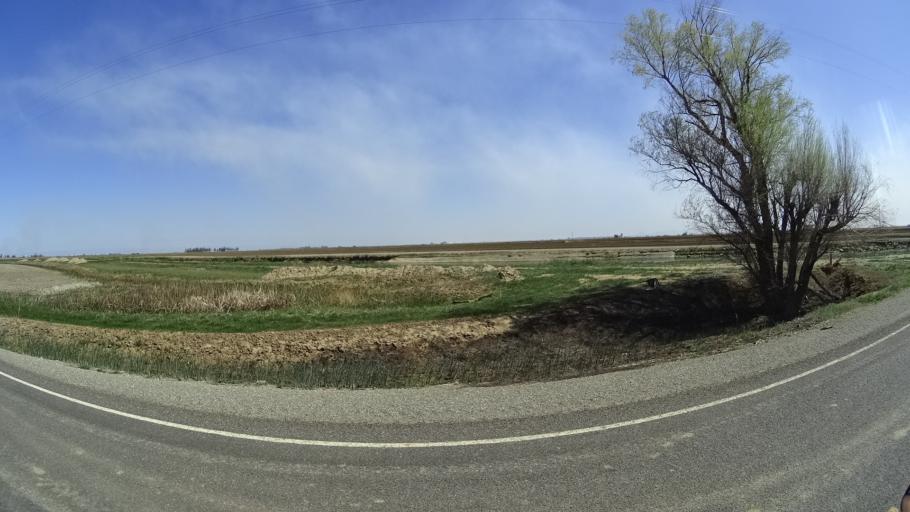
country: US
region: California
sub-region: Glenn County
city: Willows
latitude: 39.4155
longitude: -122.2484
